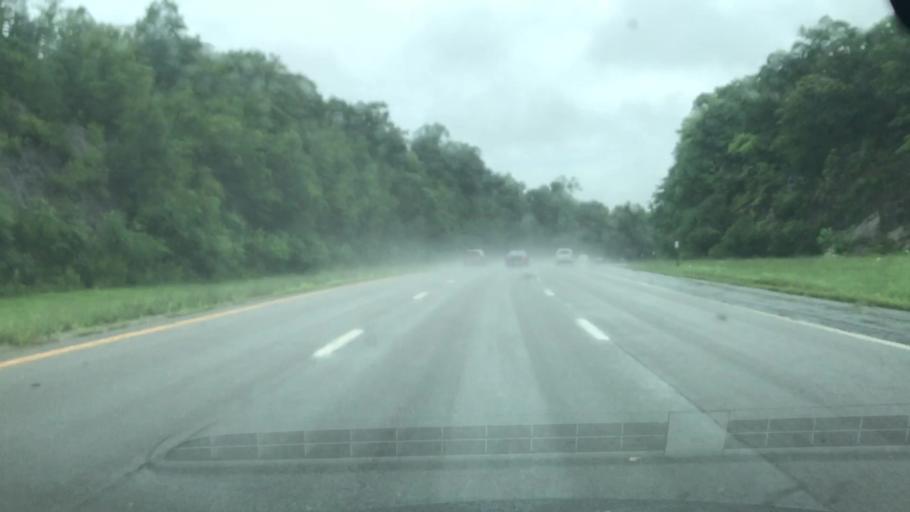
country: US
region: New York
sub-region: Westchester County
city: Yorktown Heights
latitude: 41.2172
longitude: -73.8108
